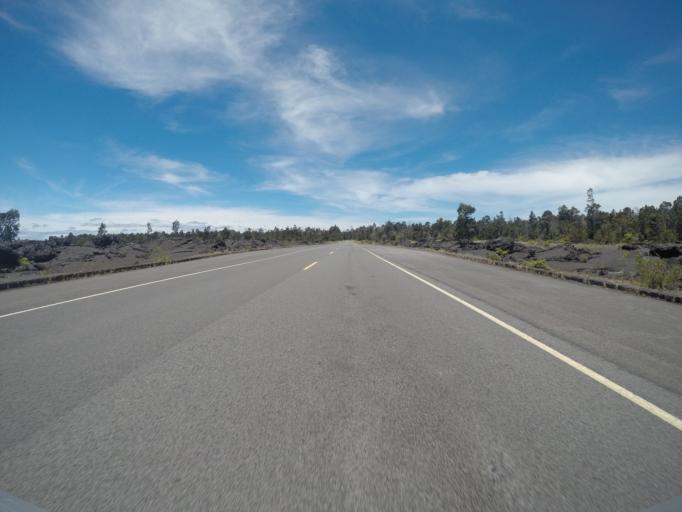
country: US
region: Hawaii
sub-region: Hawaii County
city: Volcano
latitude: 19.3613
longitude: -155.2232
